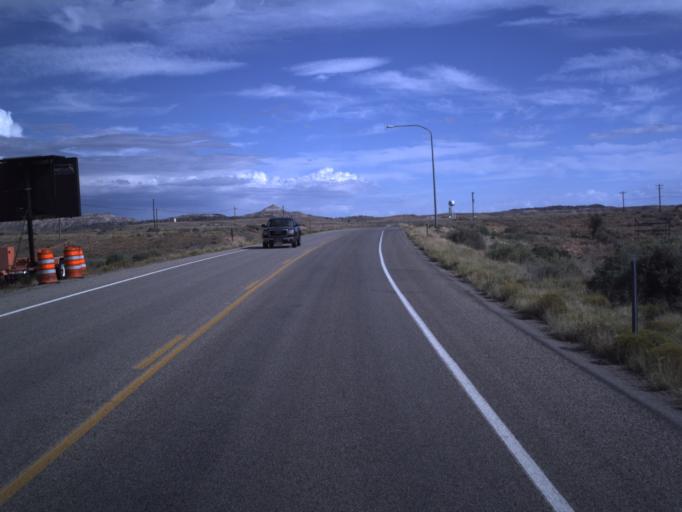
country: US
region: Colorado
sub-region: Montezuma County
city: Towaoc
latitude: 37.2079
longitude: -109.1658
